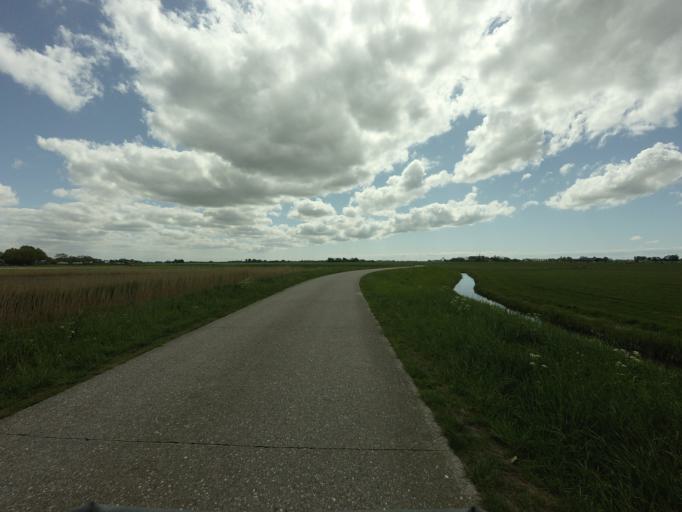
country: NL
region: Friesland
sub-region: Gemeente Littenseradiel
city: Wommels
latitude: 53.1162
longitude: 5.5508
